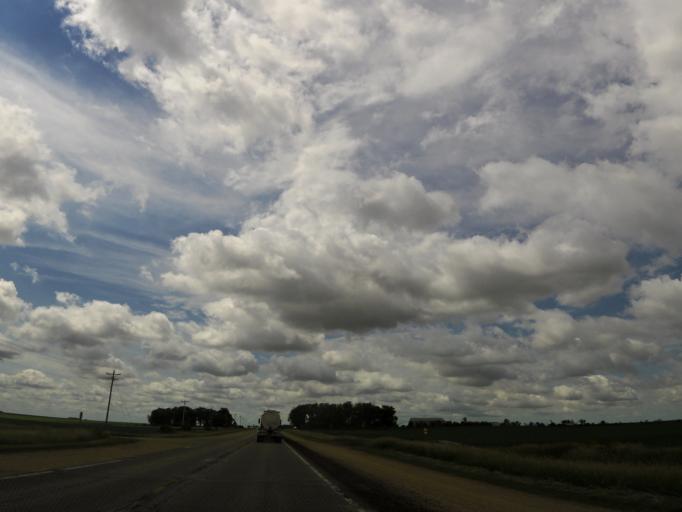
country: US
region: Iowa
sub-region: Howard County
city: Cresco
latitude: 43.3139
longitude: -92.2990
